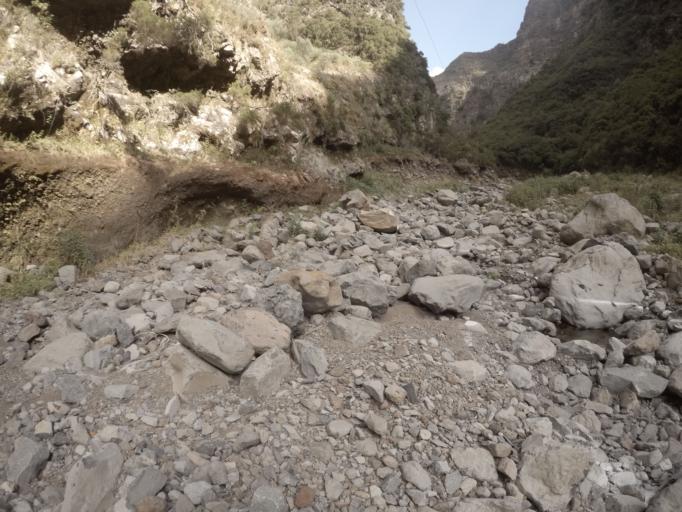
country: PT
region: Madeira
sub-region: Funchal
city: Nossa Senhora do Monte
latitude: 32.7006
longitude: -16.9204
